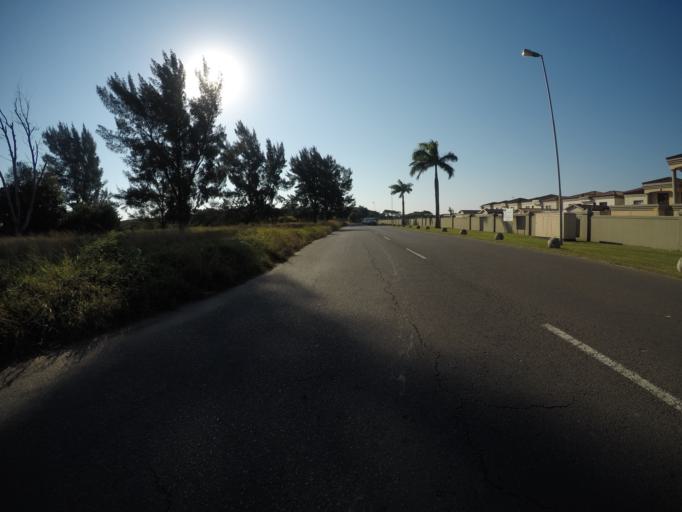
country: ZA
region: KwaZulu-Natal
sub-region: uThungulu District Municipality
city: Richards Bay
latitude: -28.7887
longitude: 32.0804
